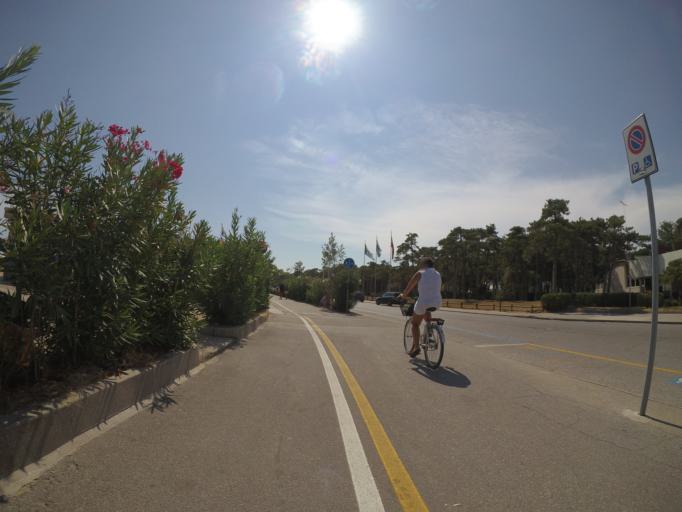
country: IT
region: Friuli Venezia Giulia
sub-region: Provincia di Udine
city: Lignano Sabbiadoro
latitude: 45.6649
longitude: 13.1101
